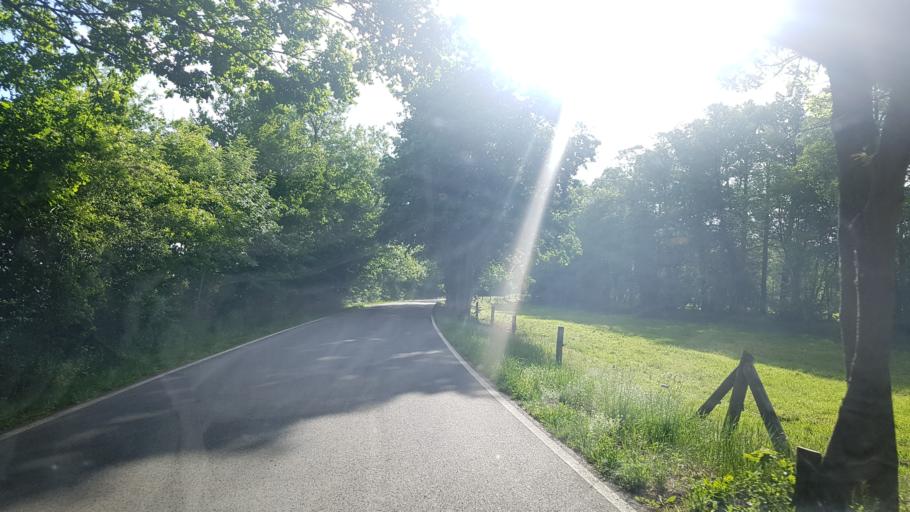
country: DE
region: Brandenburg
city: Luckau
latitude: 51.8267
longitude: 13.7345
